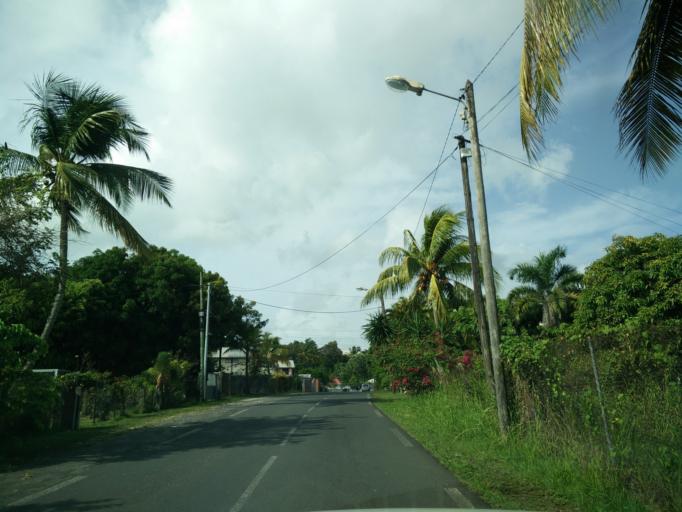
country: GP
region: Guadeloupe
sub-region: Guadeloupe
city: Les Abymes
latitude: 16.2555
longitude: -61.5158
